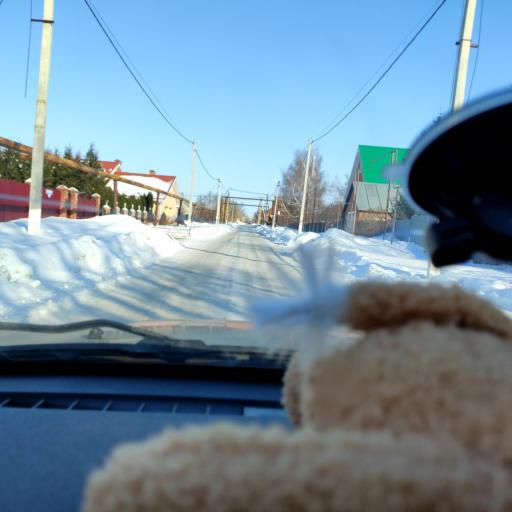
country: RU
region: Samara
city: Podstepki
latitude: 53.5151
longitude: 49.1205
